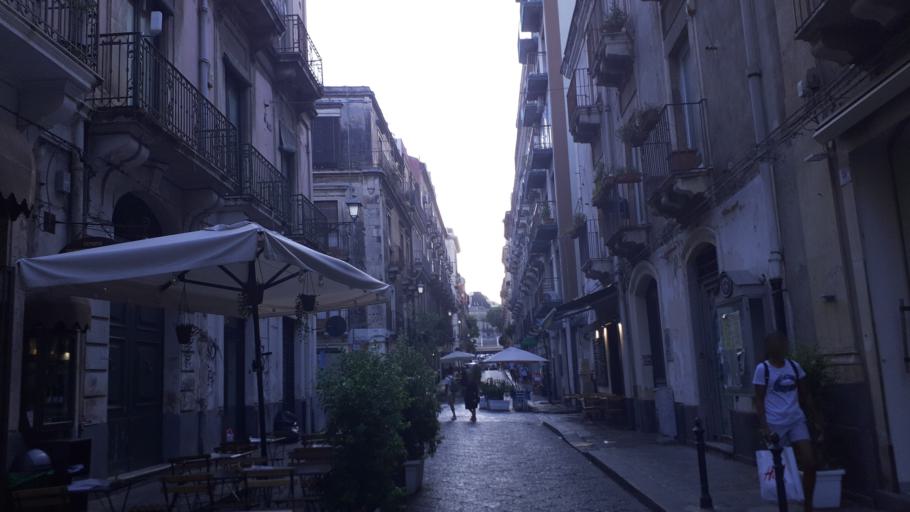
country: IT
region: Sicily
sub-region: Catania
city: Catania
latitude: 37.5098
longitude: 15.0870
